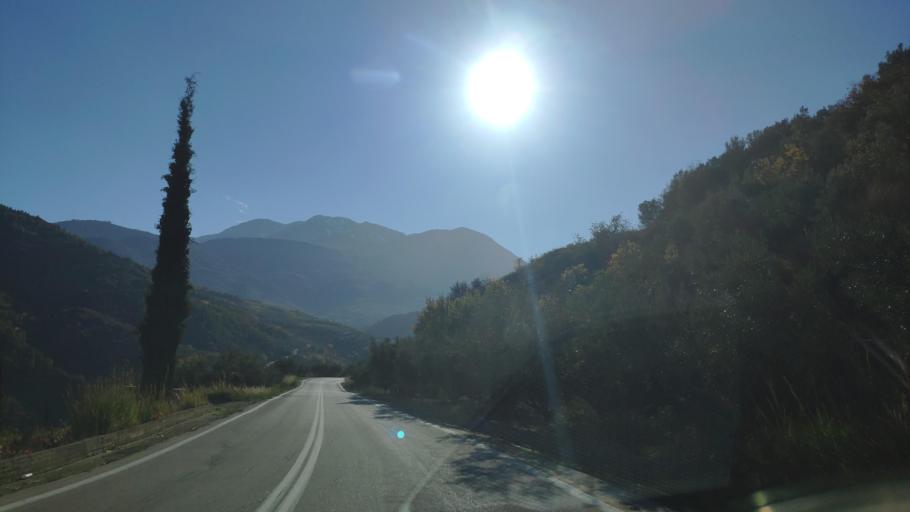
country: GR
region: Peloponnese
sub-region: Nomos Korinthias
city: Xylokastro
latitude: 38.0054
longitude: 22.5068
